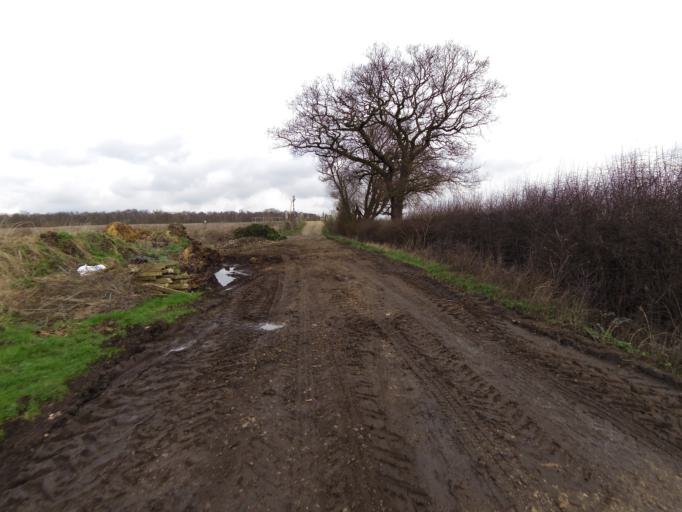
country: GB
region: England
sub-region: Doncaster
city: Askern
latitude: 53.5804
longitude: -1.1326
